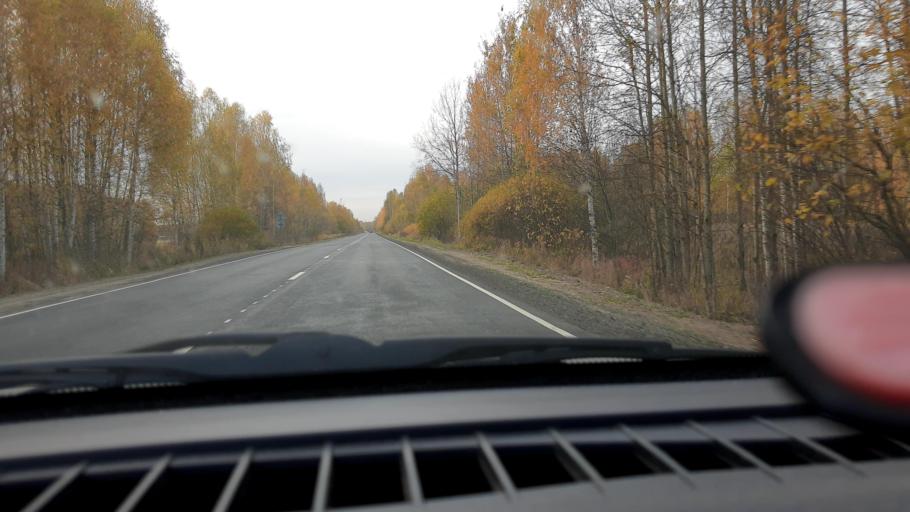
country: RU
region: Nizjnij Novgorod
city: Lukino
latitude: 56.5362
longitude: 43.7850
